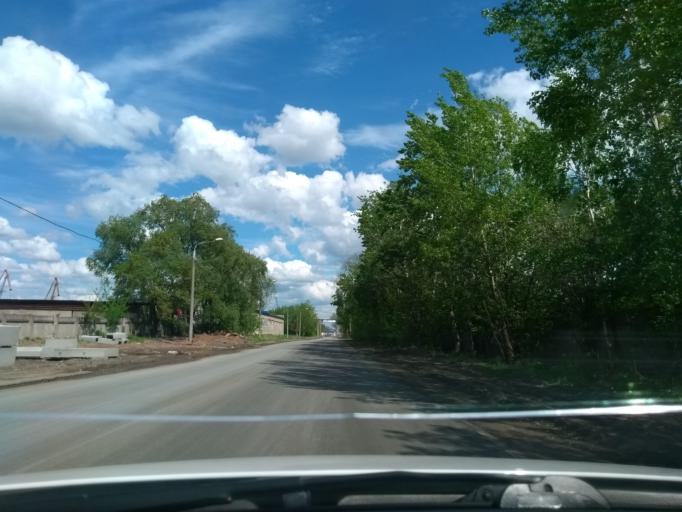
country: RU
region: Perm
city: Kondratovo
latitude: 58.0081
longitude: 56.0905
